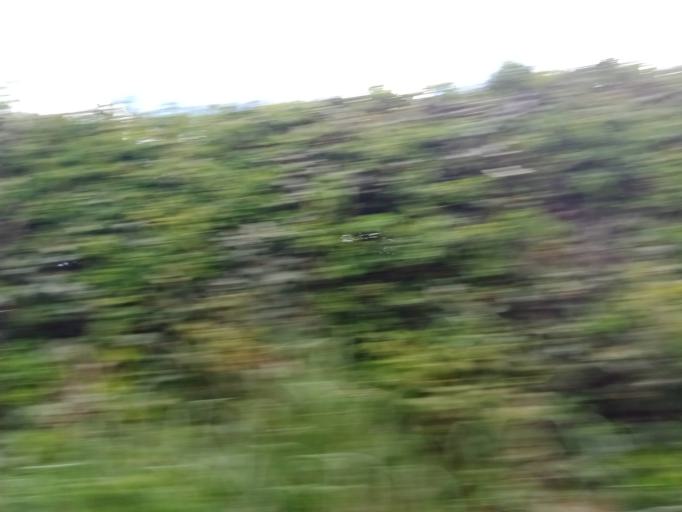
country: IE
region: Munster
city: Thurles
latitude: 52.6728
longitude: -7.6769
